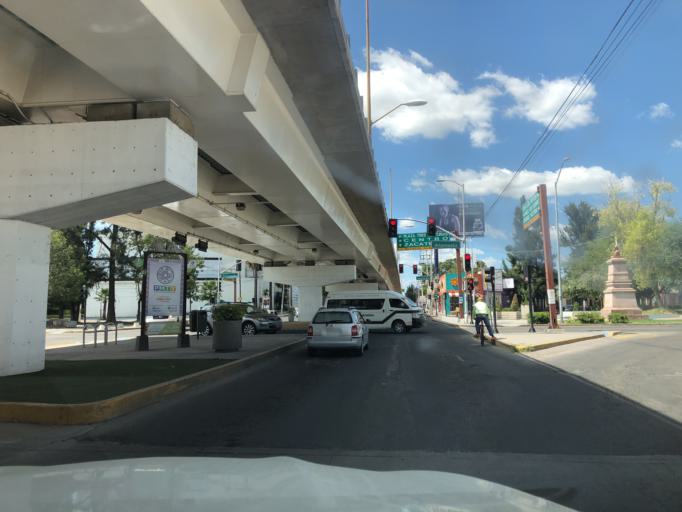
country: MX
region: Aguascalientes
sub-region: Aguascalientes
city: Aguascalientes
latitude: 21.8835
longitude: -102.2724
